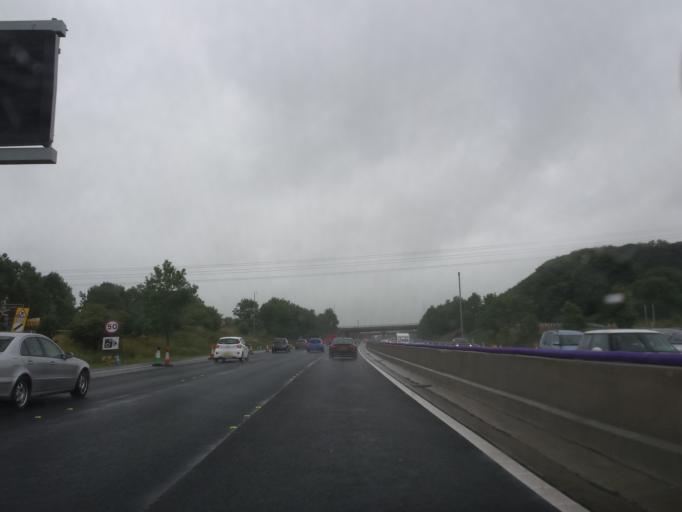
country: GB
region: England
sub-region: Derbyshire
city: Bolsover
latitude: 53.2013
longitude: -1.3218
